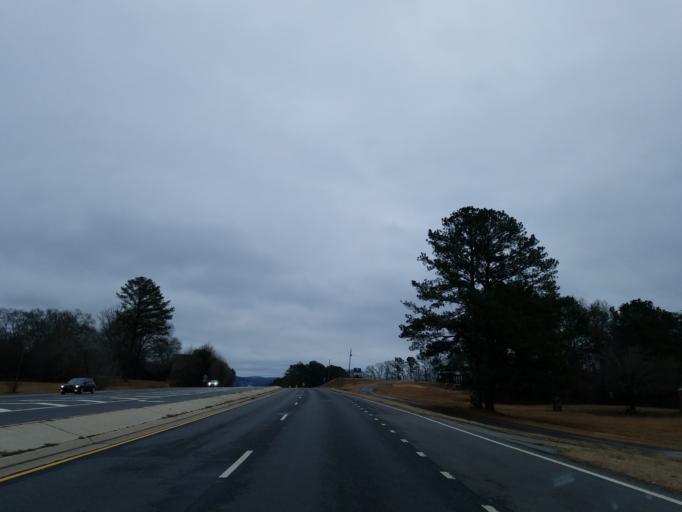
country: US
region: Georgia
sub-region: Bartow County
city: Cartersville
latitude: 34.2098
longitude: -84.8282
